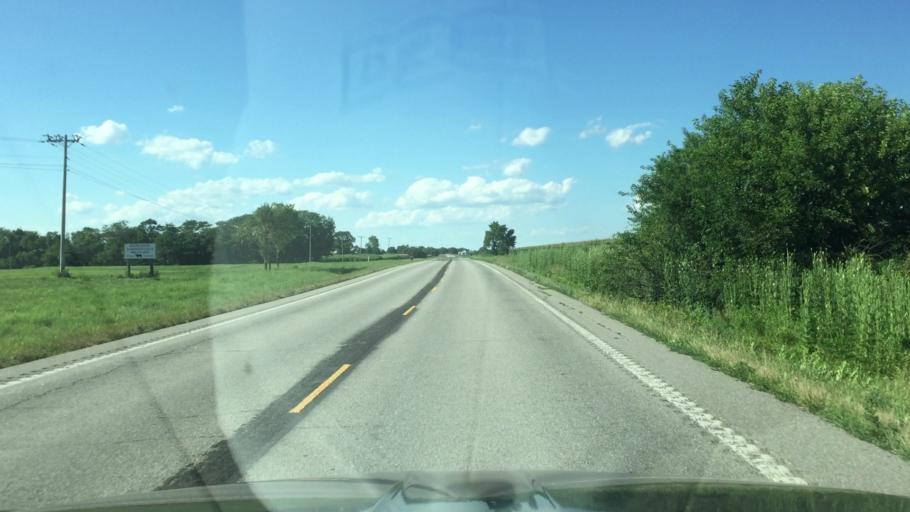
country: US
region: Missouri
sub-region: Moniteau County
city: Tipton
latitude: 38.5923
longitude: -92.7891
